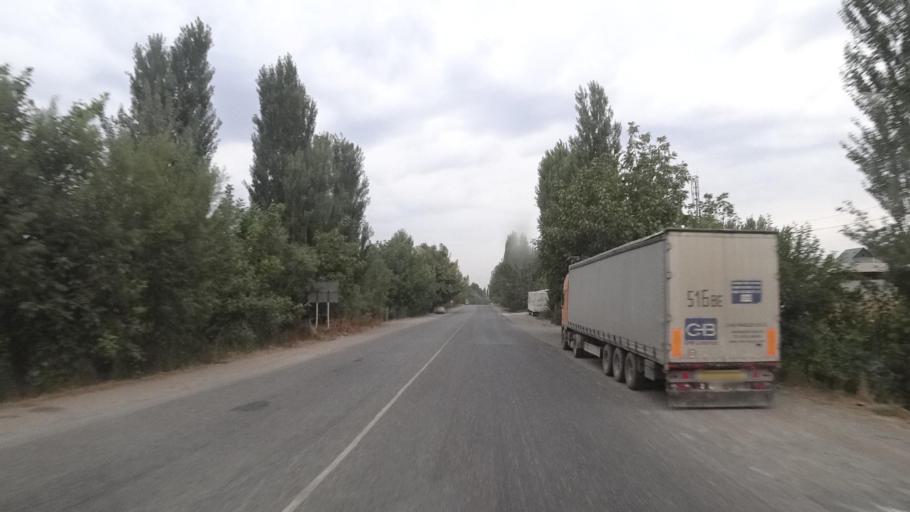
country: UZ
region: Namangan
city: Haqqulobod Shahri
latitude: 41.0492
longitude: 72.3096
